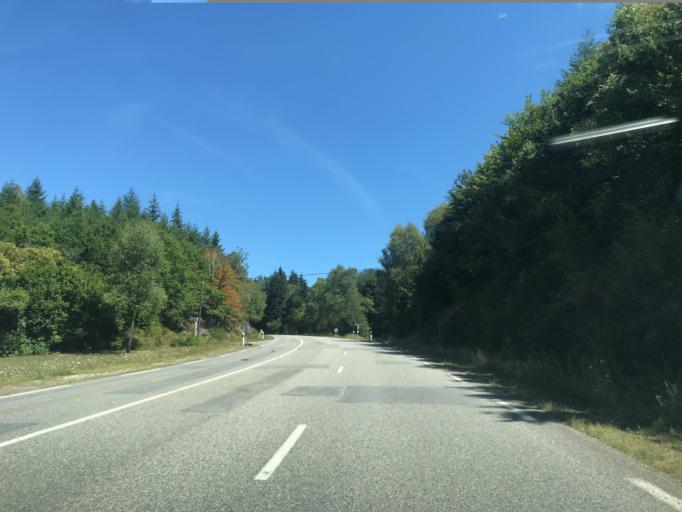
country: FR
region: Limousin
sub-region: Departement de la Correze
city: Meymac
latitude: 45.4715
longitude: 2.1672
